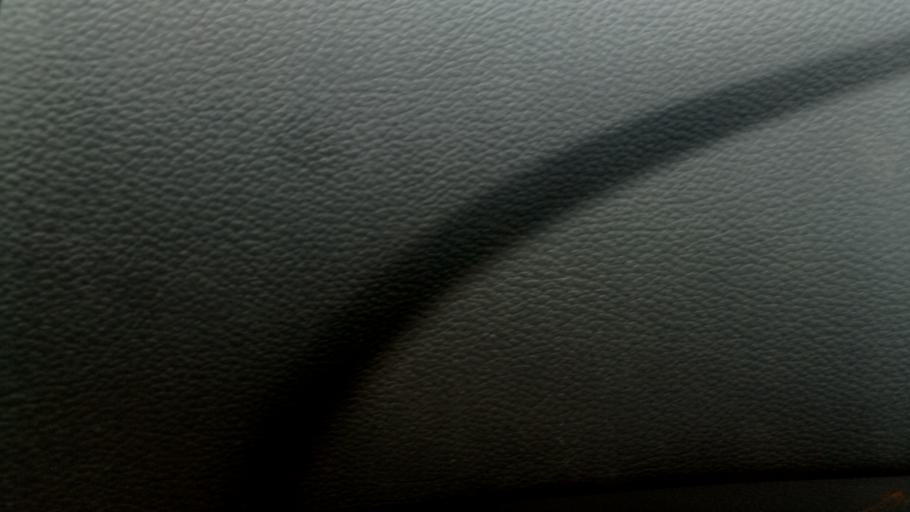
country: CD
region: Katanga
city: Lubumbashi
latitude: -11.5826
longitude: 27.5185
